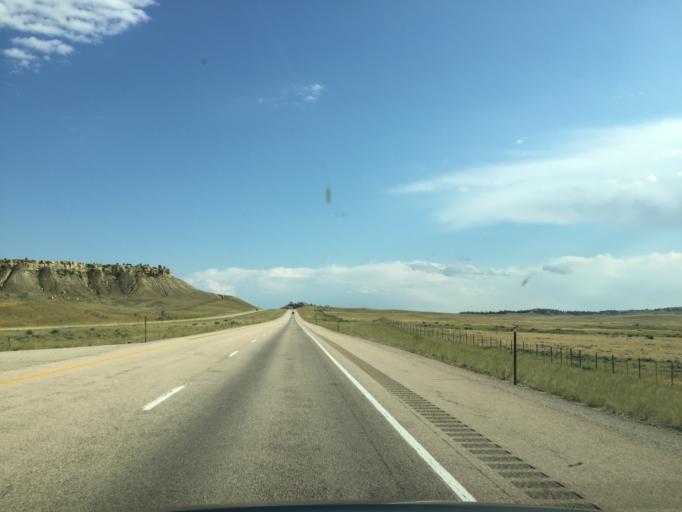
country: US
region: Wyoming
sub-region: Natrona County
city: Bar Nunn
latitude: 43.2692
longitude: -106.3909
